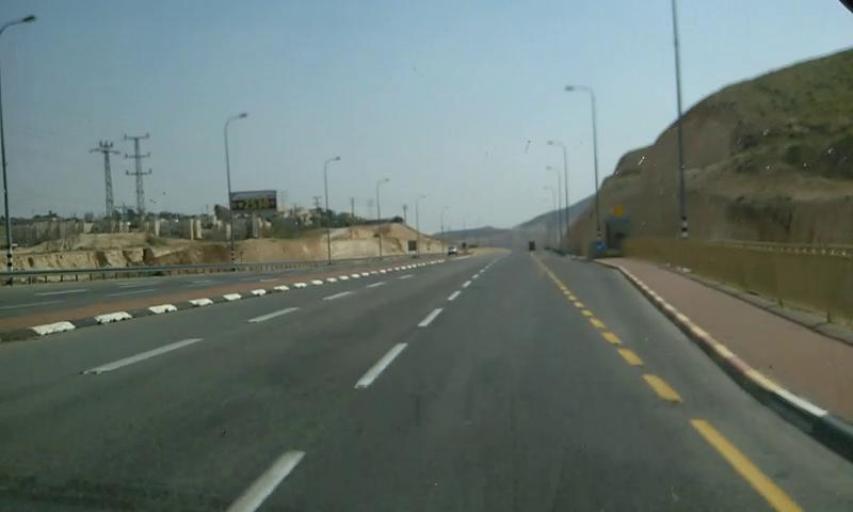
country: PS
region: West Bank
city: Jericho
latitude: 31.8179
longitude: 35.3894
